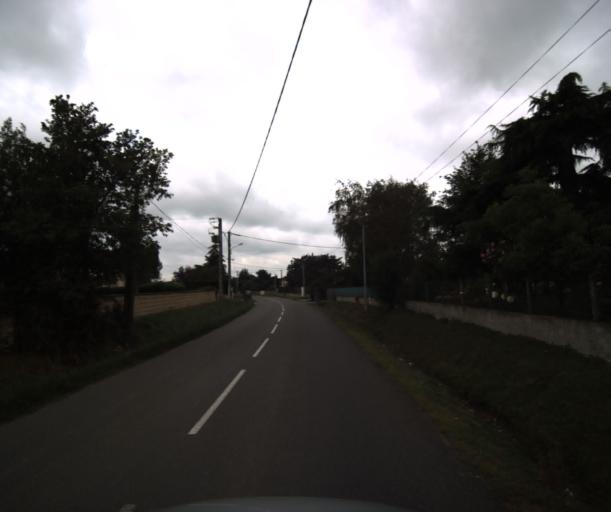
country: FR
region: Midi-Pyrenees
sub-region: Departement de la Haute-Garonne
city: Seysses
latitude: 43.4522
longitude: 1.3004
